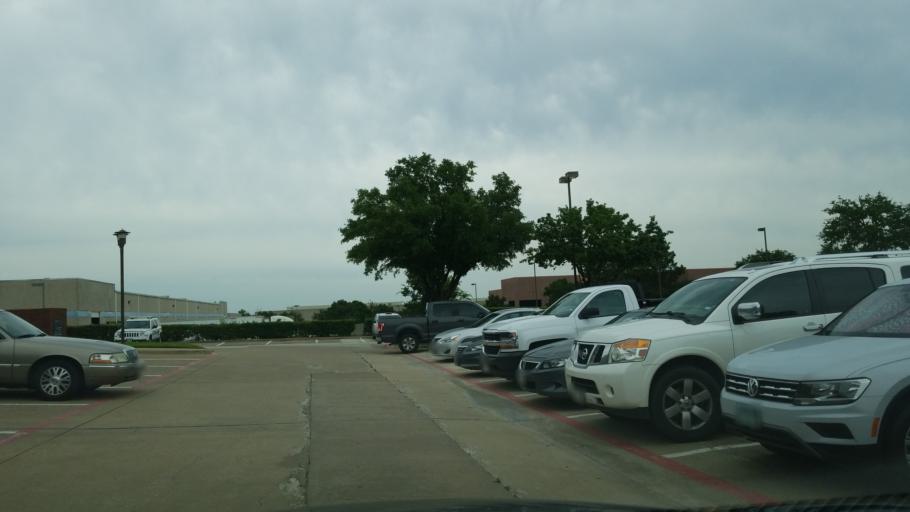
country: US
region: Texas
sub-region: Dallas County
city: Coppell
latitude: 32.8952
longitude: -96.9881
